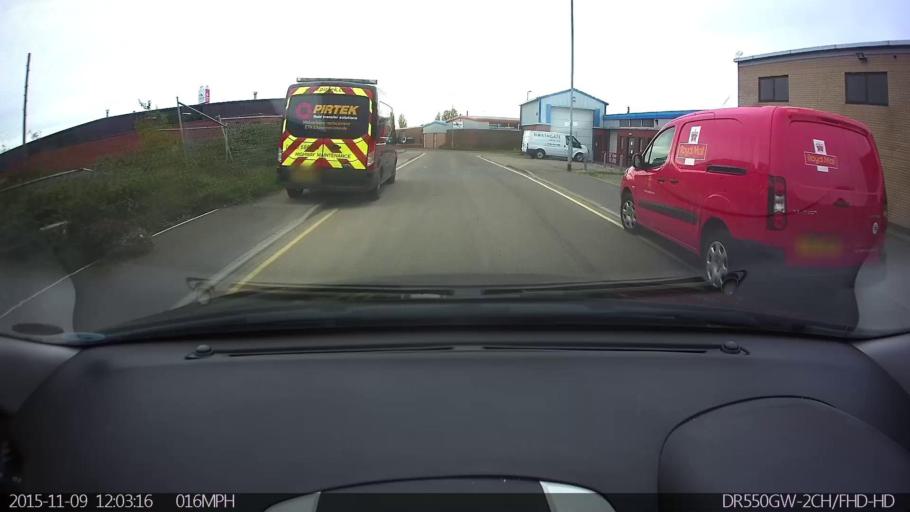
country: GB
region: England
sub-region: Essex
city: Little Clacton
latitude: 51.8194
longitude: 1.1662
